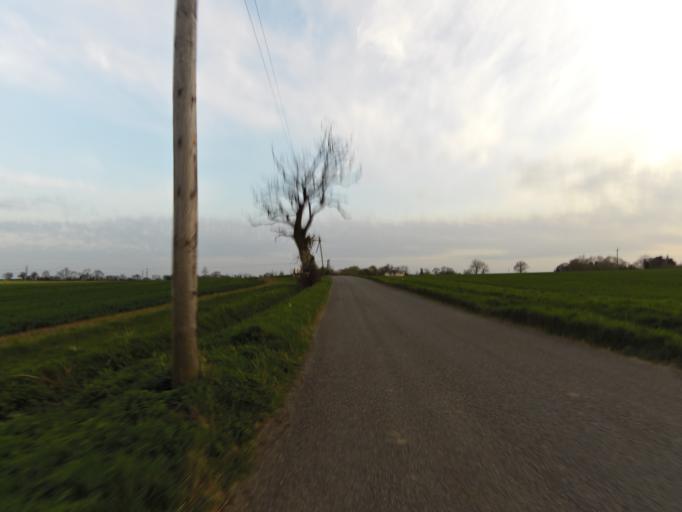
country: GB
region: England
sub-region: Suffolk
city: Kesgrave
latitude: 52.1258
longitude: 1.2291
